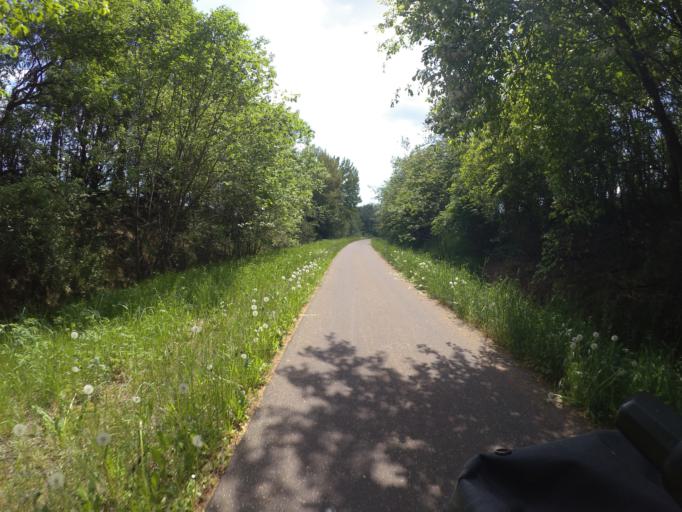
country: DE
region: Rheinland-Pfalz
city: Scheid
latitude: 50.3639
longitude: 6.3864
